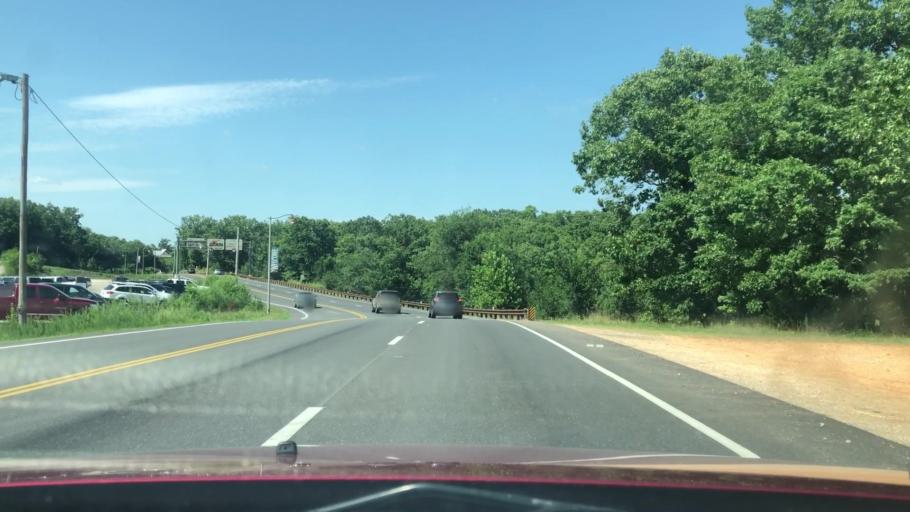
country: US
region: Missouri
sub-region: Stone County
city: Kimberling City
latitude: 36.6633
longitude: -93.3368
